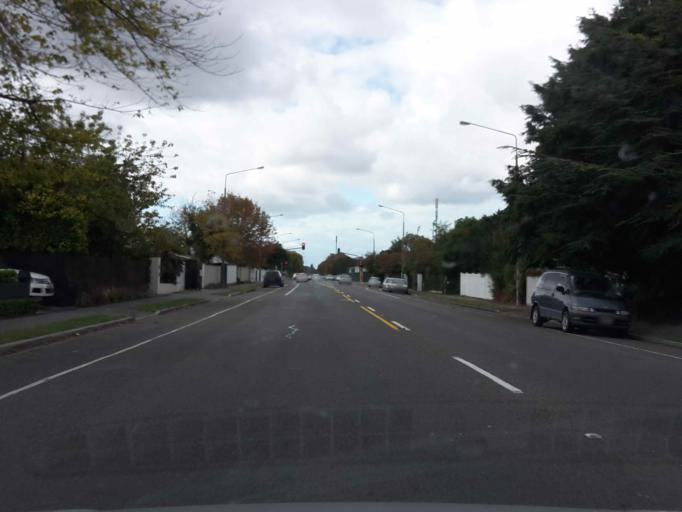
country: NZ
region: Canterbury
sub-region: Christchurch City
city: Christchurch
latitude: -43.5061
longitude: 172.6256
